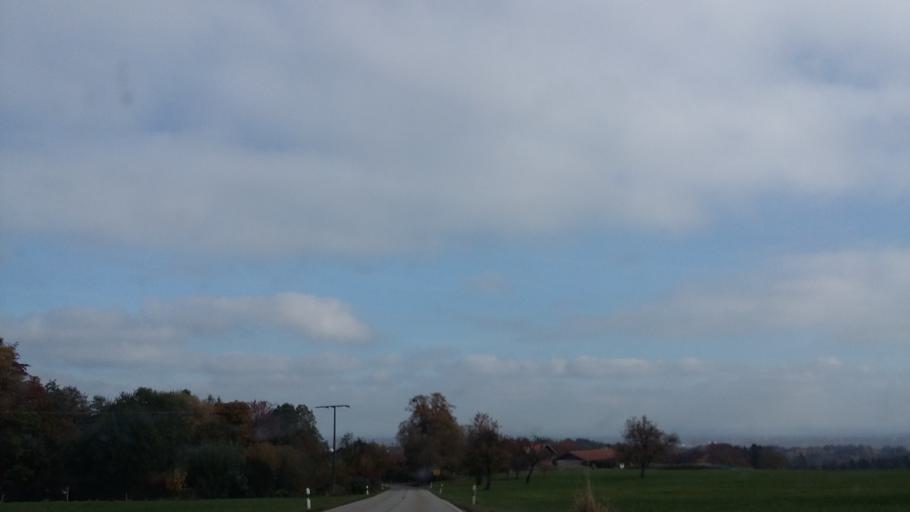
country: DE
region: Bavaria
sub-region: Upper Bavaria
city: Irschenberg
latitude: 47.8430
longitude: 11.9293
